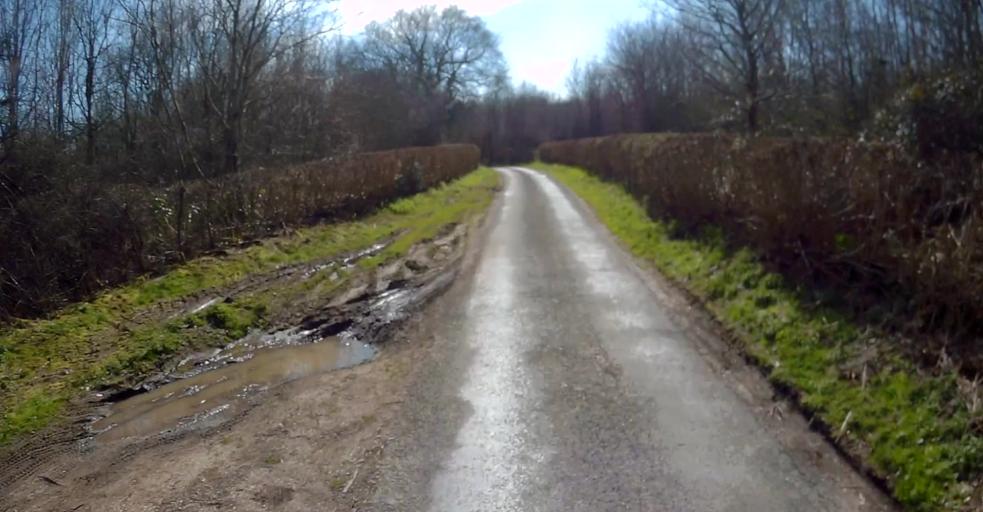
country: GB
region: England
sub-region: Hampshire
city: Four Marks
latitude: 51.1742
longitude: -1.0637
